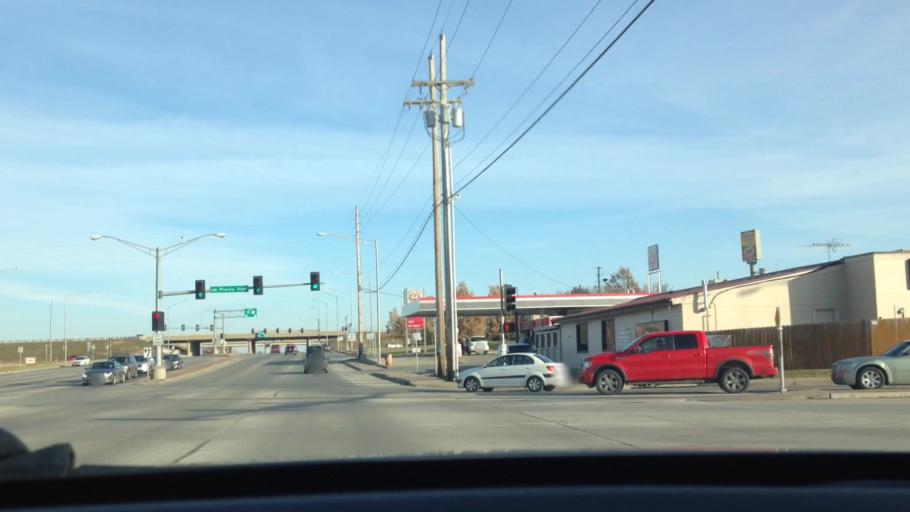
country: US
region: Missouri
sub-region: Platte County
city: Weatherby Lake
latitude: 39.2468
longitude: -94.6618
